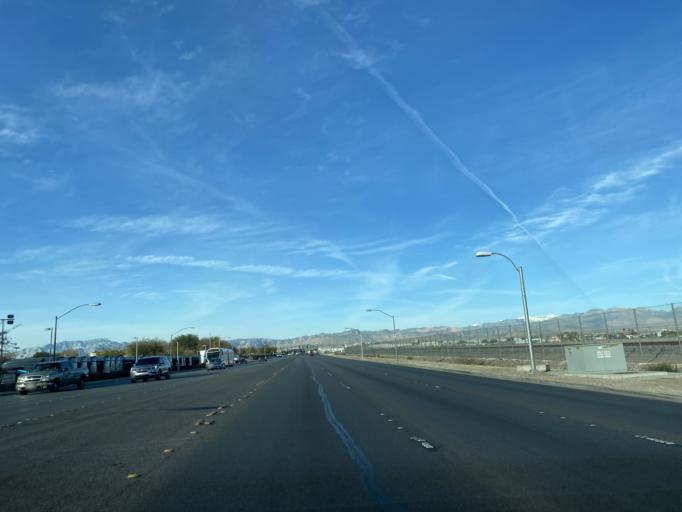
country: US
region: Nevada
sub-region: Clark County
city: Paradise
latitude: 36.0712
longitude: -115.1669
